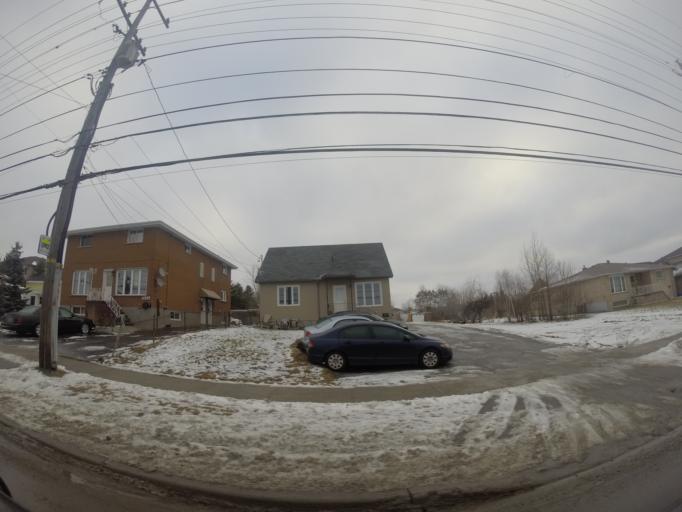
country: CA
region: Ontario
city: Greater Sudbury
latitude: 46.4636
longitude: -81.0280
